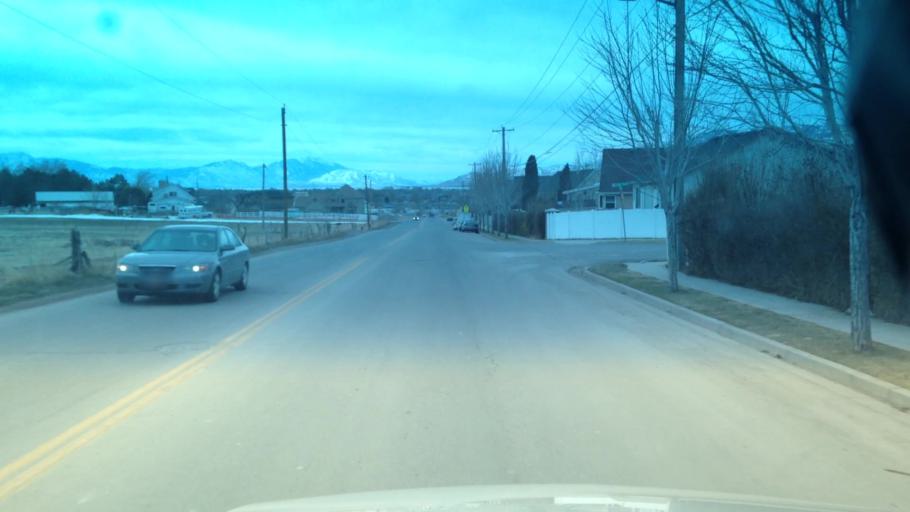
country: US
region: Utah
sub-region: Utah County
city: Lehi
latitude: 40.4254
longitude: -111.8689
